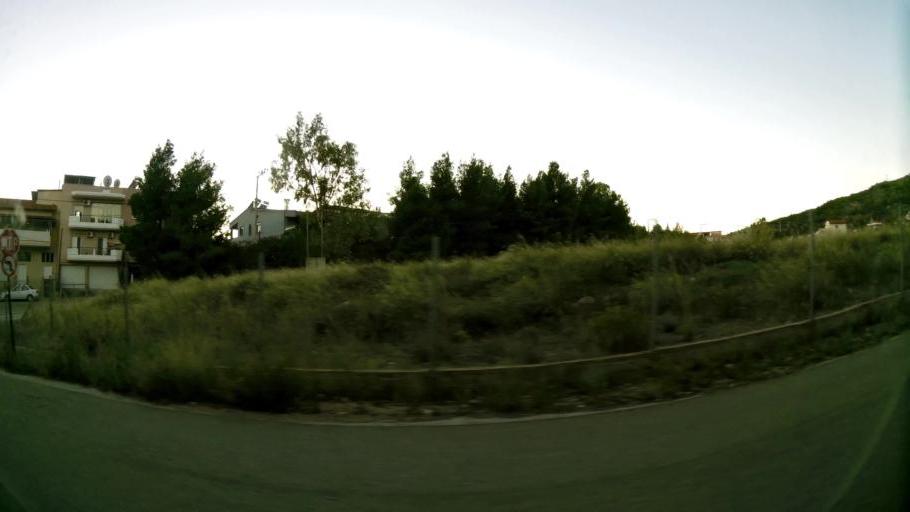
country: GR
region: Attica
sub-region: Nomarchia Dytikis Attikis
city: Ano Liosia
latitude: 38.0945
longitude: 23.7006
